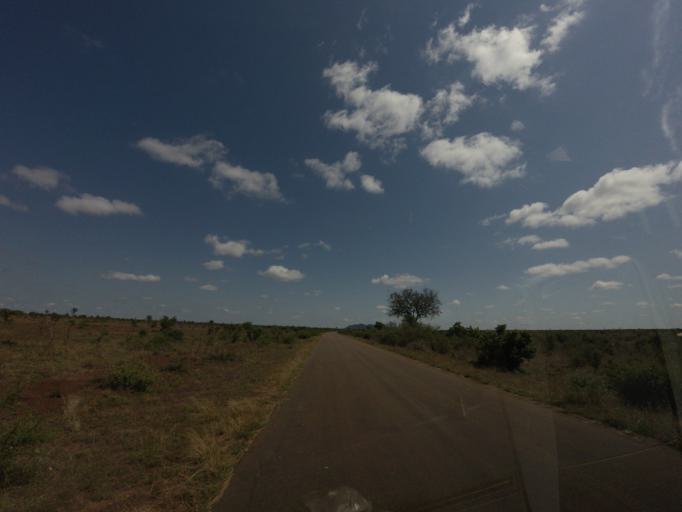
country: ZA
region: Mpumalanga
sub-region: Ehlanzeni District
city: Komatipoort
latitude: -25.0924
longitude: 31.9188
